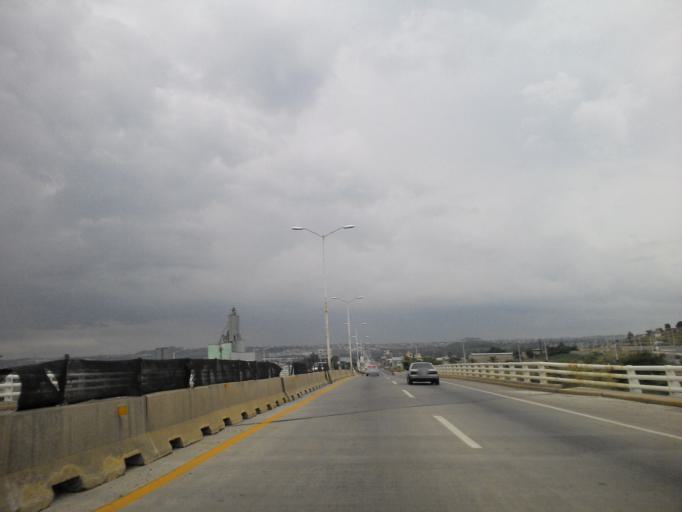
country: MX
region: Jalisco
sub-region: Tonala
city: Colonia Guadalupana
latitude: 20.5784
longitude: -103.2172
